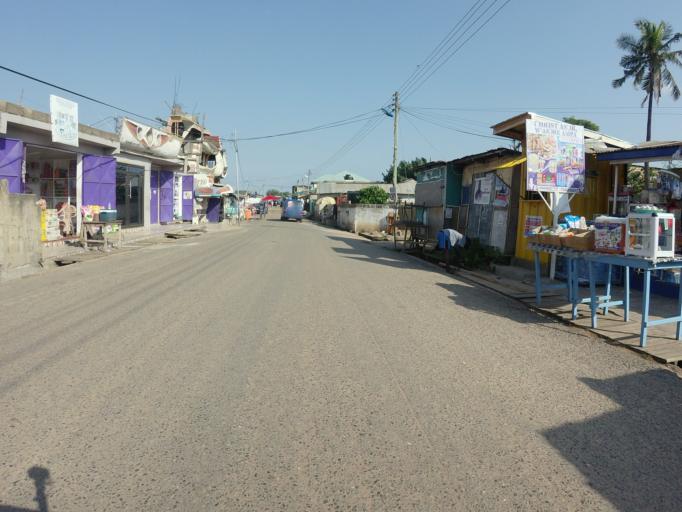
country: GH
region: Greater Accra
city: Dome
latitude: 5.6131
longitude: -0.2343
